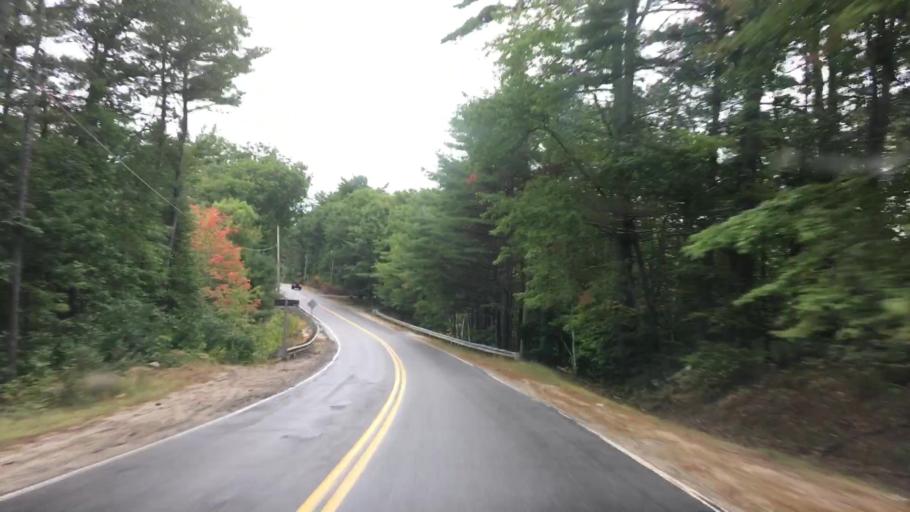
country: US
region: Maine
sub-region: Cumberland County
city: Raymond
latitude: 43.9492
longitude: -70.4627
